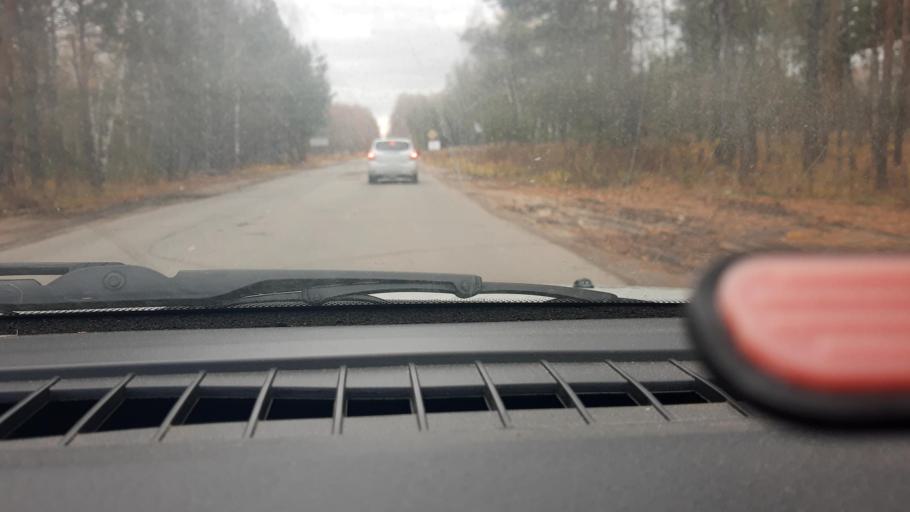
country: RU
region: Nizjnij Novgorod
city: Babino
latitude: 56.3023
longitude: 43.6638
